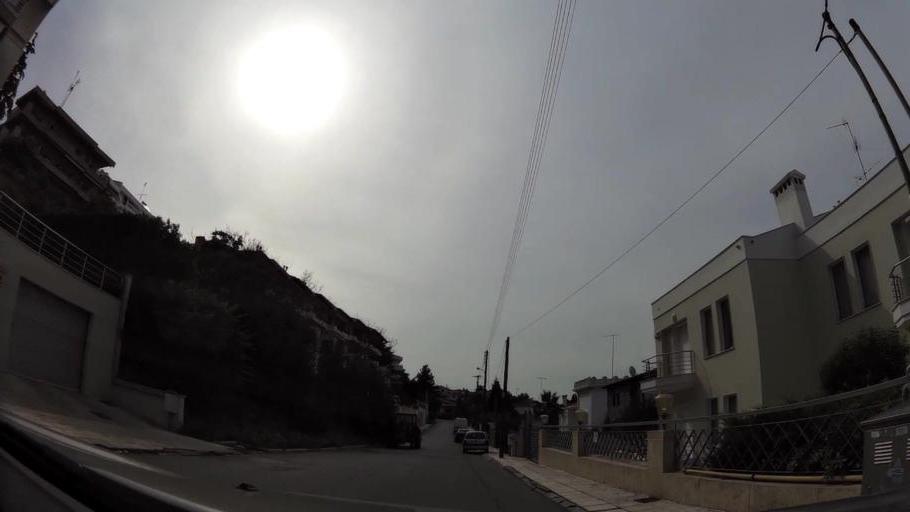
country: GR
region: Central Macedonia
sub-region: Nomos Thessalonikis
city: Panorama
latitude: 40.5852
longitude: 23.0290
